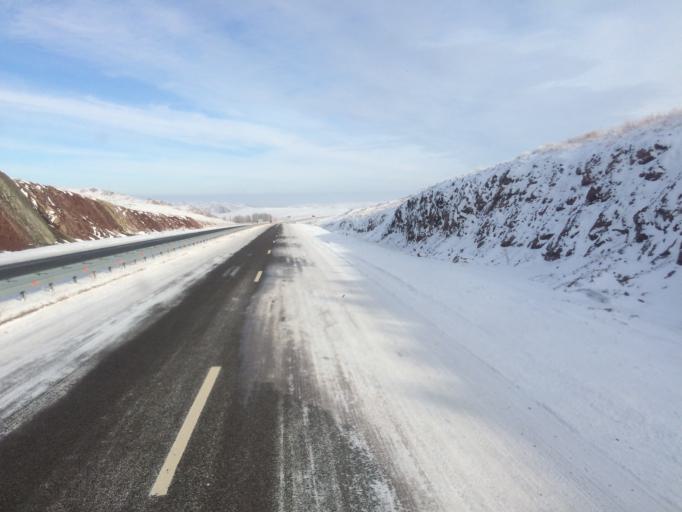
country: KZ
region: Zhambyl
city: Georgiyevka
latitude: 43.4311
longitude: 74.9114
